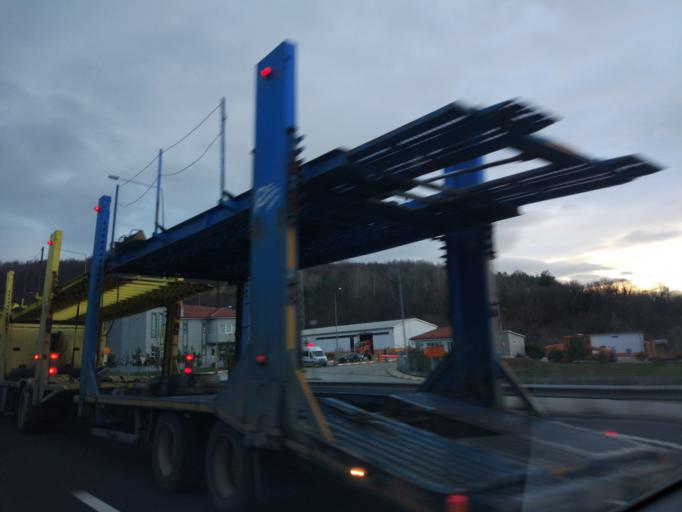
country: TR
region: Duzce
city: Kaynasli
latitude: 40.7348
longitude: 31.4470
